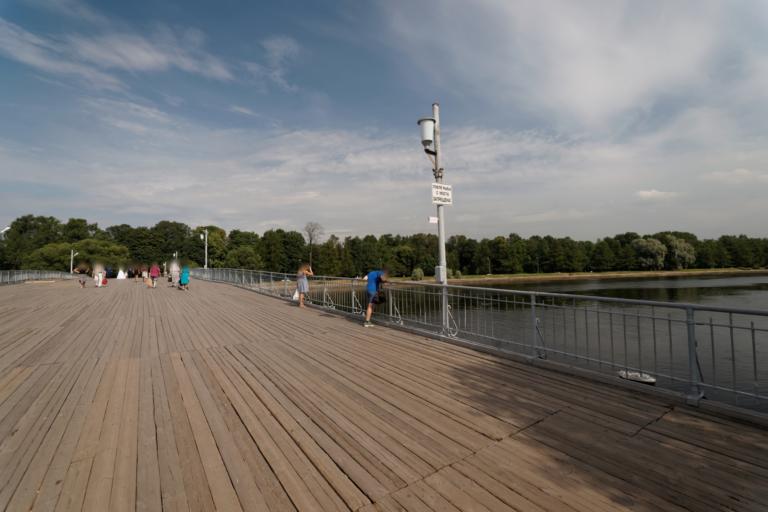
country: RU
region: Leningrad
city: Krestovskiy ostrov
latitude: 59.9750
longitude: 30.2582
